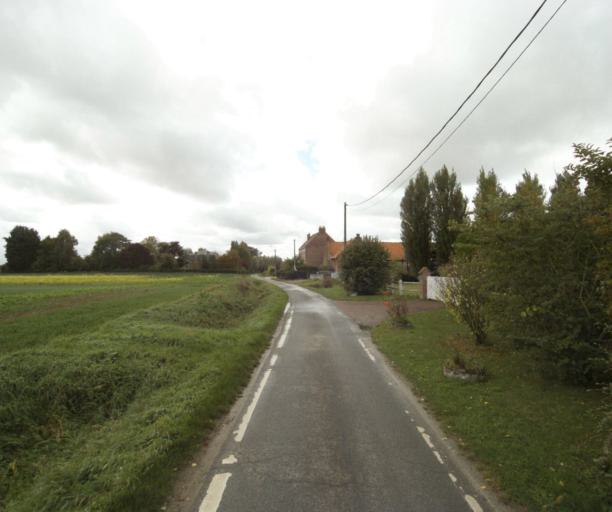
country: FR
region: Nord-Pas-de-Calais
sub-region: Departement du Nord
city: Houplines
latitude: 50.6698
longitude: 2.9273
